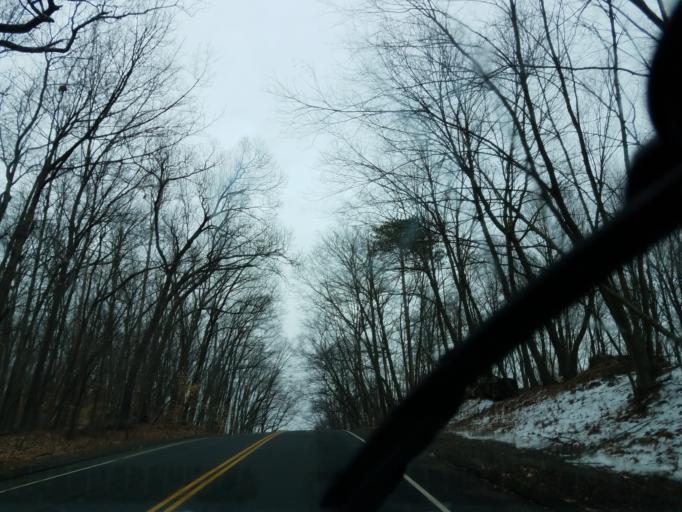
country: US
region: Connecticut
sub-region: Hartford County
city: New Britain
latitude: 41.6961
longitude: -72.7803
